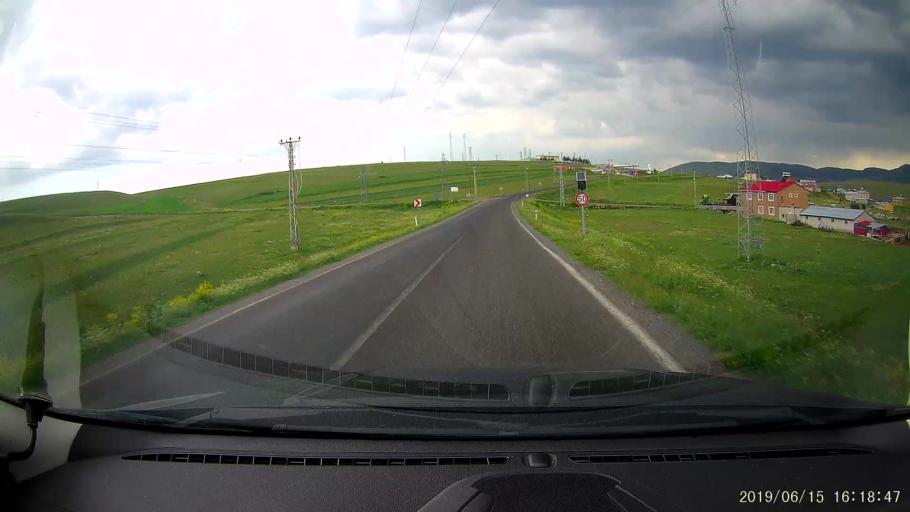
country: TR
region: Ardahan
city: Hanak
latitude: 41.2357
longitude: 42.8534
